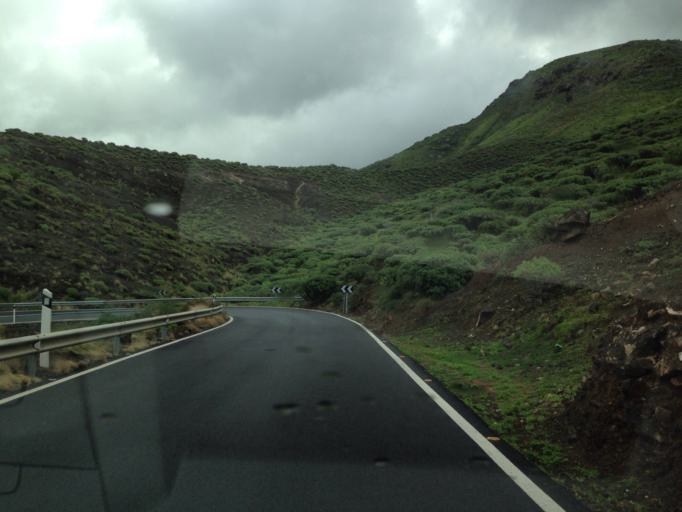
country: ES
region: Canary Islands
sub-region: Provincia de Las Palmas
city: Agaete
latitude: 28.0926
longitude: -15.7004
